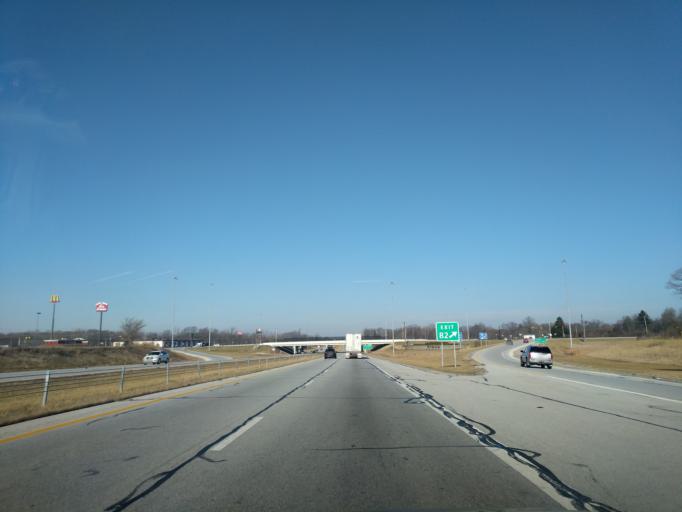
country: US
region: Ohio
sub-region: Miami County
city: Piqua
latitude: 40.1481
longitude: -84.2192
